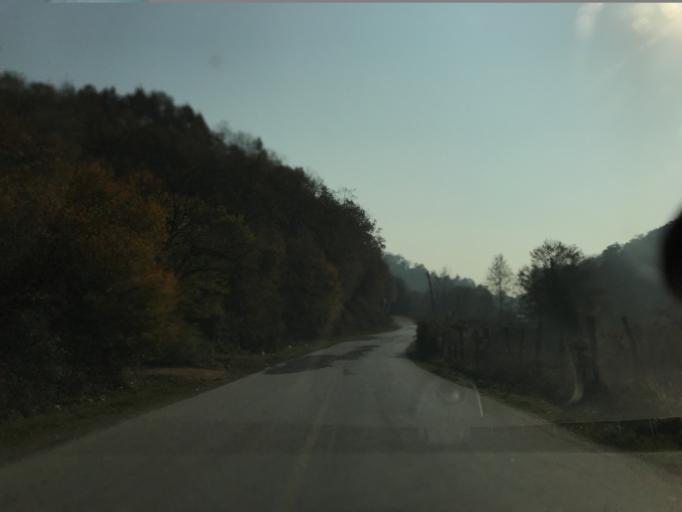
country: TR
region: Duzce
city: Cumayeri
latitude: 40.8959
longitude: 30.9542
